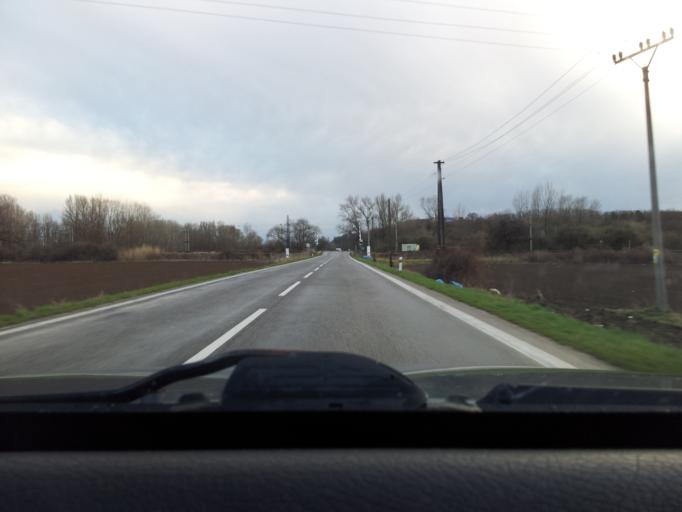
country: SK
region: Nitriansky
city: Tlmace
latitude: 48.3019
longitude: 18.5325
